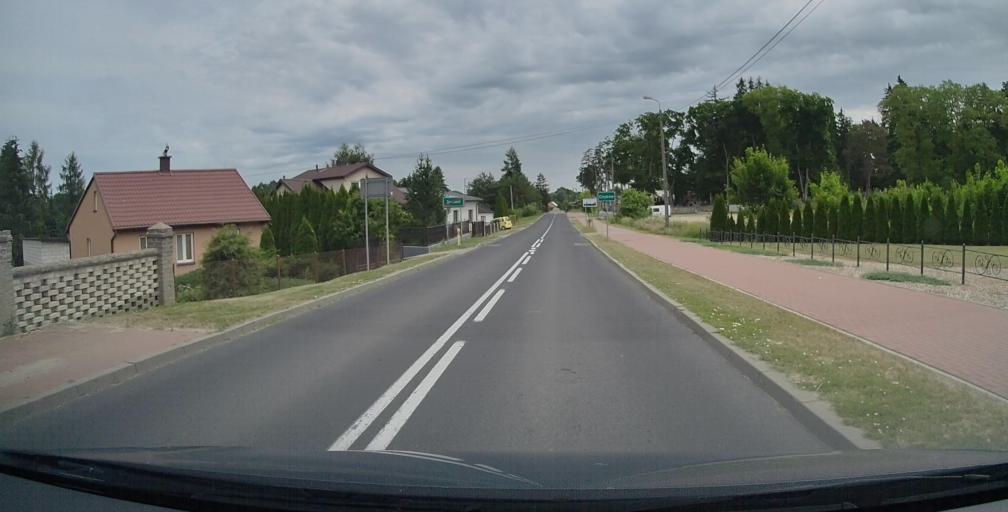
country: PL
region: Masovian Voivodeship
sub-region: Powiat losicki
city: Sarnaki
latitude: 52.3127
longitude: 22.8943
